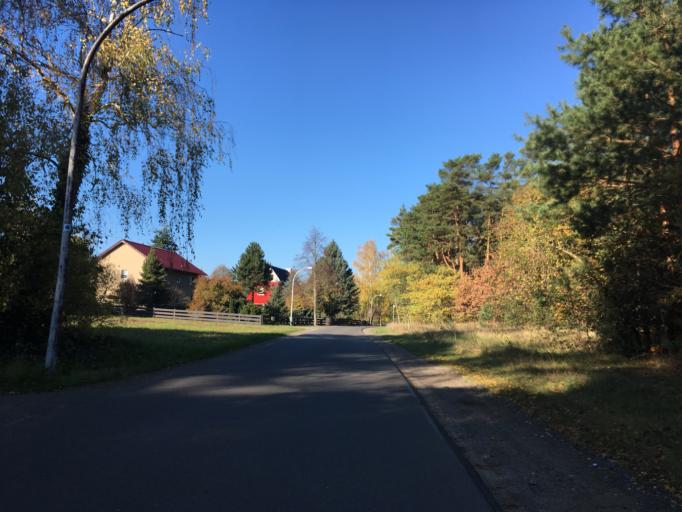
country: DE
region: Brandenburg
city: Reichenwalde
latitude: 52.2899
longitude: 14.0081
